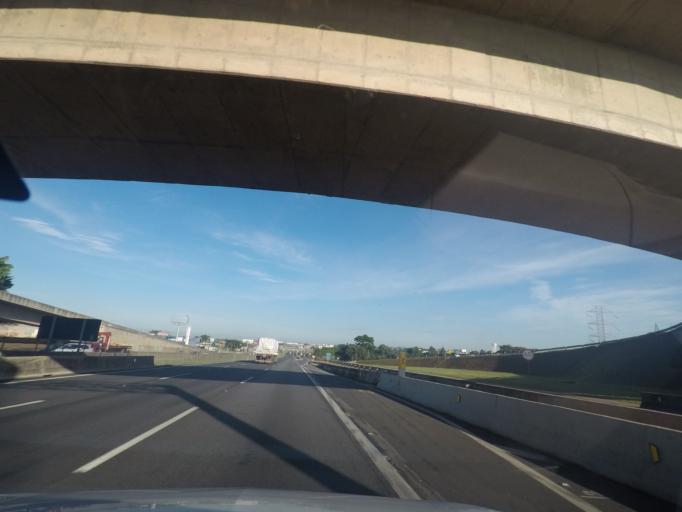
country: BR
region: Sao Paulo
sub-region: Hortolandia
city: Hortolandia
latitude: -22.8273
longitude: -47.1840
